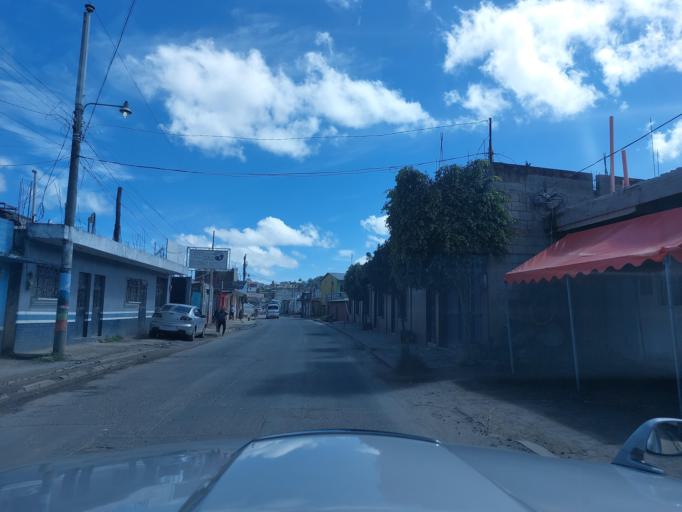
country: GT
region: Chimaltenango
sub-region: Municipio de San Juan Comalapa
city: Comalapa
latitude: 14.7289
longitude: -90.8873
